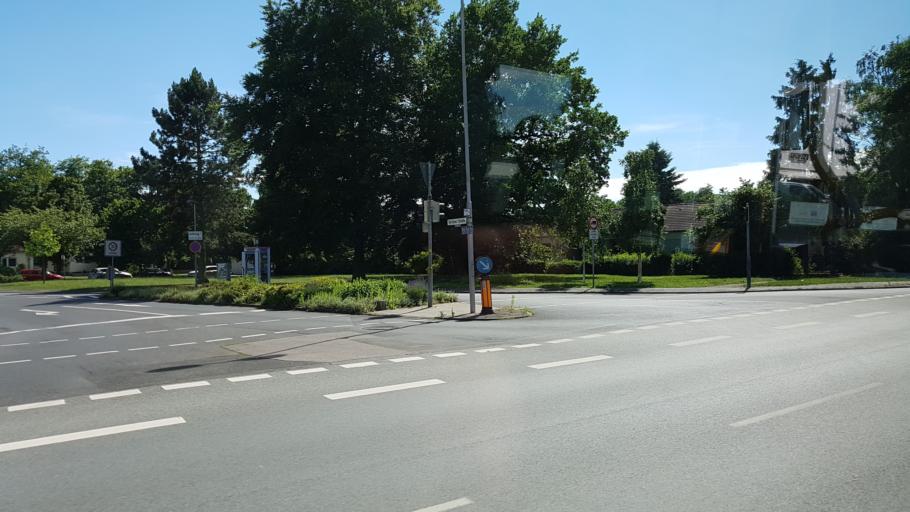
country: DE
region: Hesse
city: Heusenstamm
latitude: 50.0588
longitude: 8.7847
